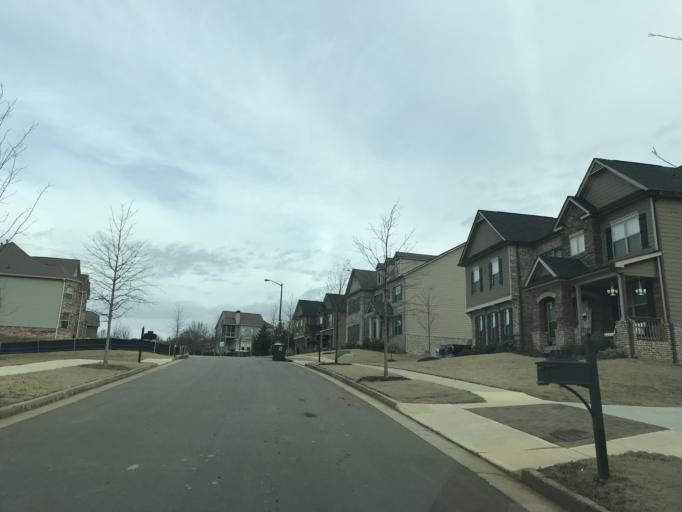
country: US
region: Georgia
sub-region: Cherokee County
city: Canton
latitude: 34.2018
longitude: -84.4002
